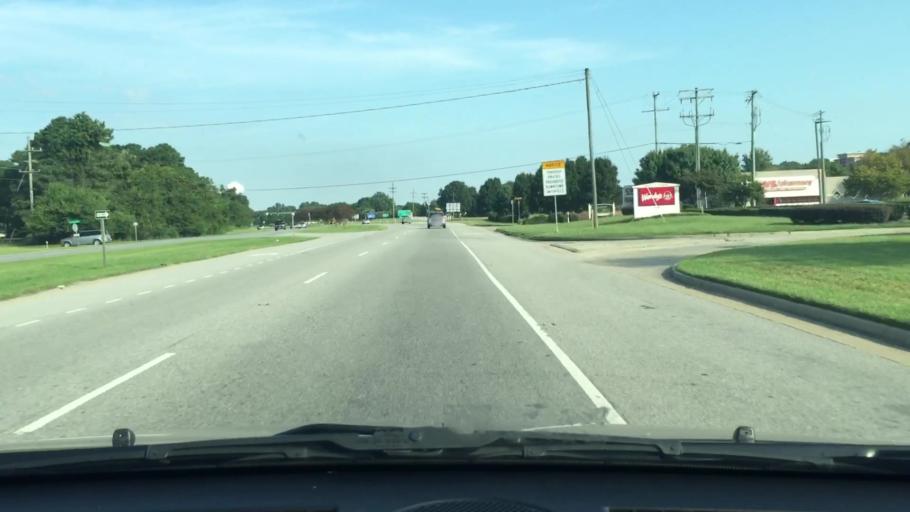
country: US
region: Virginia
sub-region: Isle of Wight County
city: Smithfield
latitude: 36.9580
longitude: -76.6029
